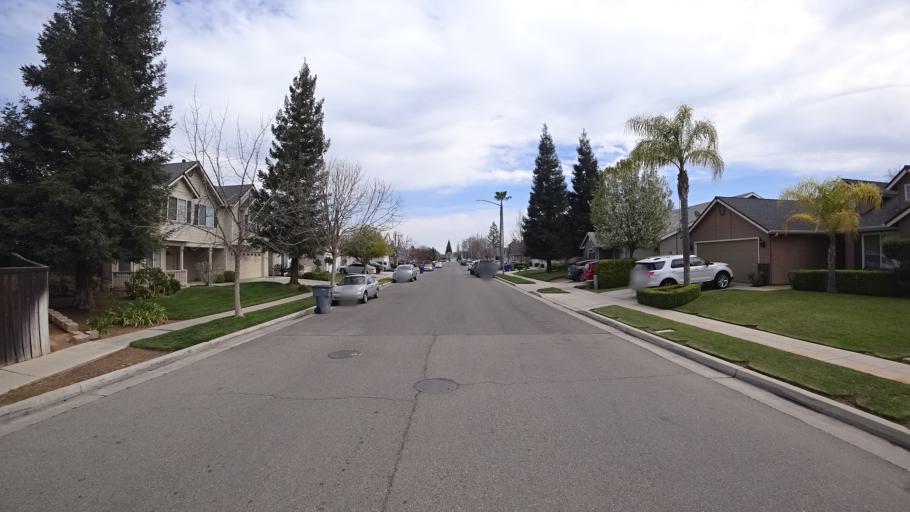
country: US
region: California
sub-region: Fresno County
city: Biola
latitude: 36.8301
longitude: -119.8986
